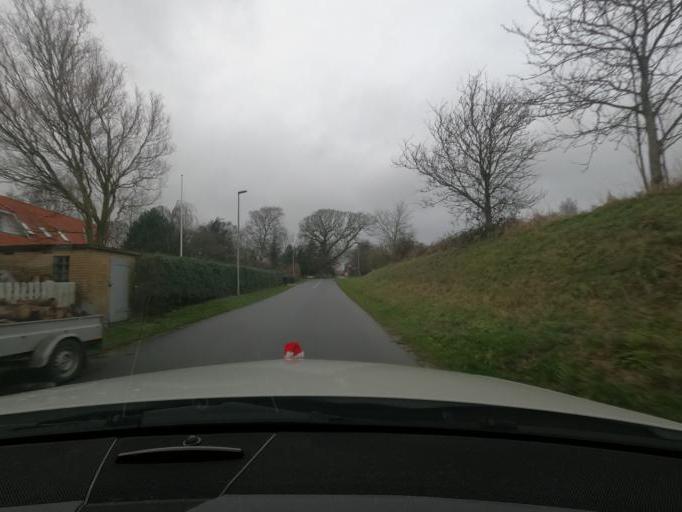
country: DK
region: South Denmark
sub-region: Haderslev Kommune
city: Starup
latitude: 55.2014
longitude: 9.6396
